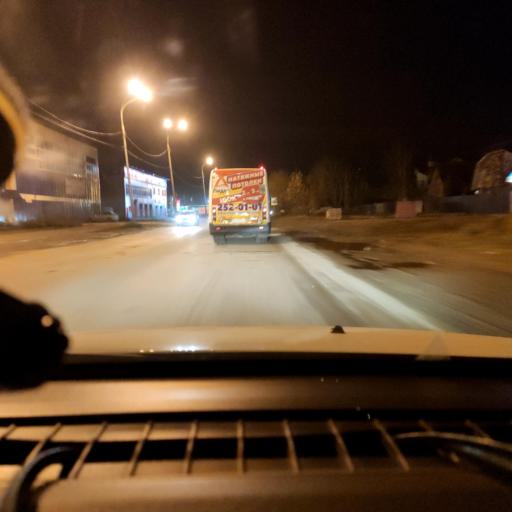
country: RU
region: Samara
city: Samara
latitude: 53.1333
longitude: 50.1204
